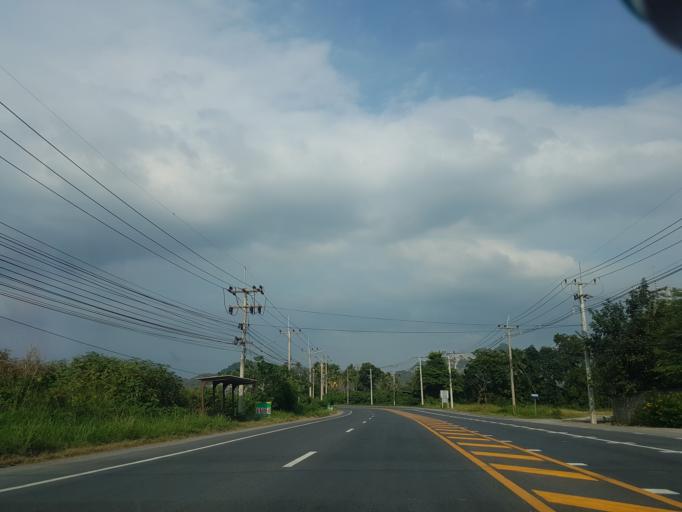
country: TH
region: Sara Buri
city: Phra Phutthabat
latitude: 14.6692
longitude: 100.7720
